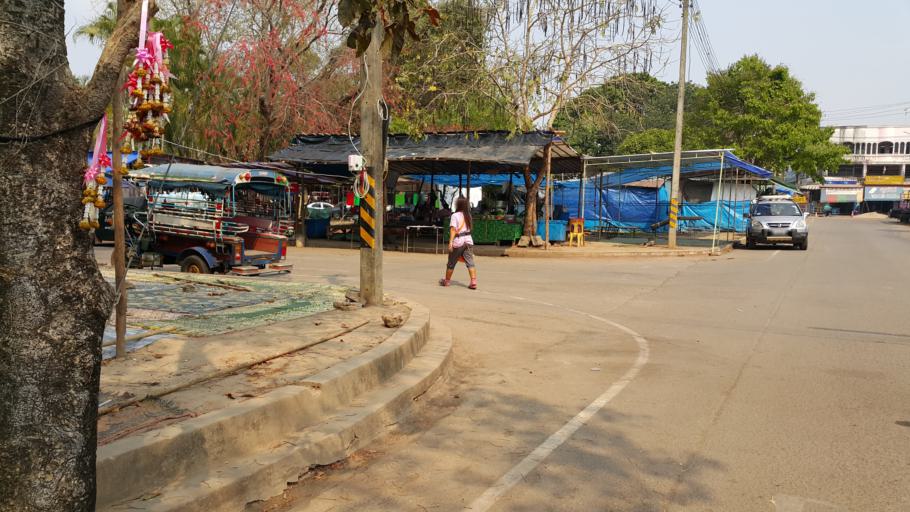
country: TH
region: Nakhon Phanom
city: That Phanom
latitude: 16.9412
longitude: 104.7236
